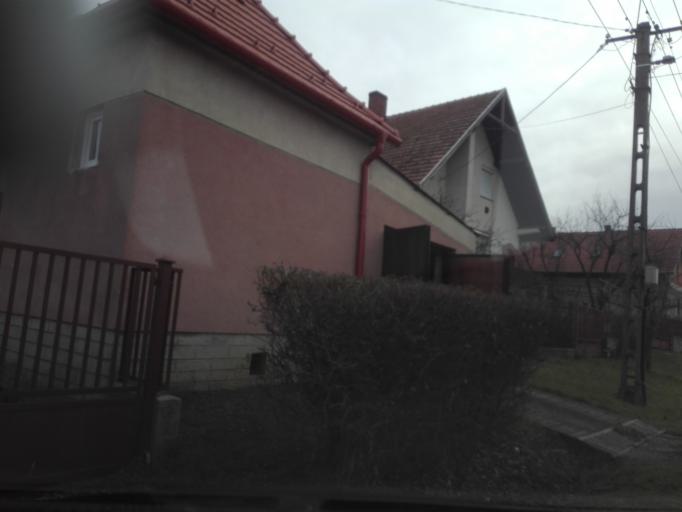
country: HU
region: Veszprem
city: Balatonfured
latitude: 47.0068
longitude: 17.7967
